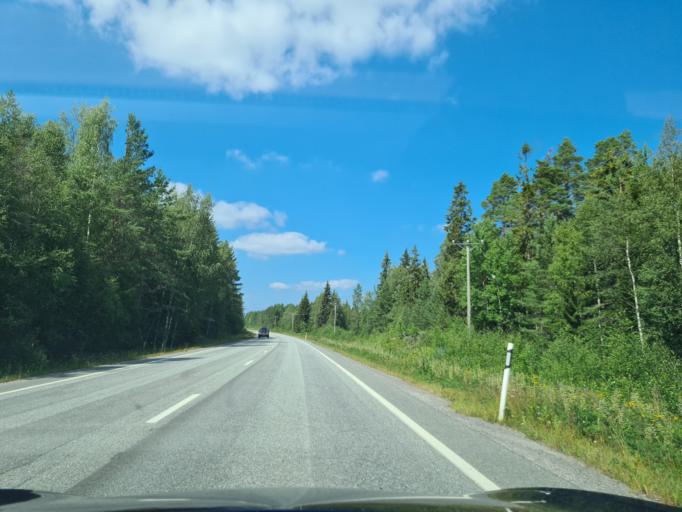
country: FI
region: Ostrobothnia
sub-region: Vaasa
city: Vaasa
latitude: 63.1778
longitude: 21.5759
